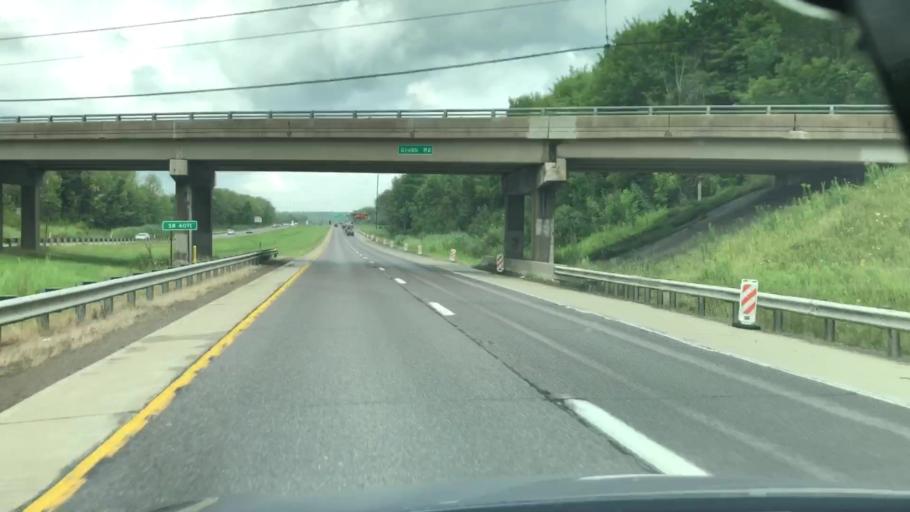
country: US
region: Pennsylvania
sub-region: Erie County
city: Fairview
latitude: 42.0158
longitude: -80.1427
